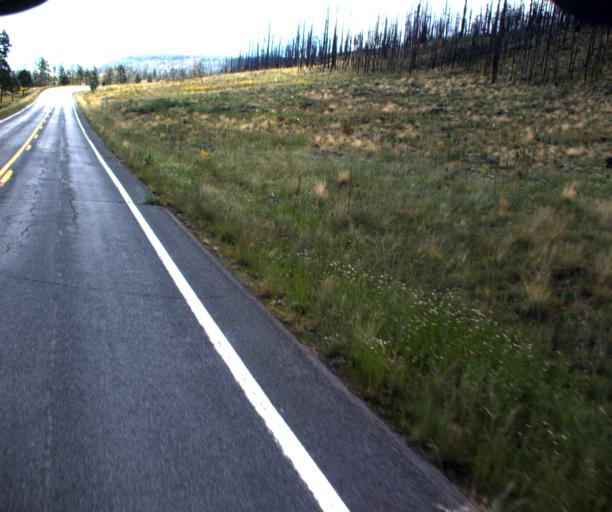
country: US
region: Arizona
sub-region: Apache County
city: Eagar
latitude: 34.0540
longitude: -109.3516
